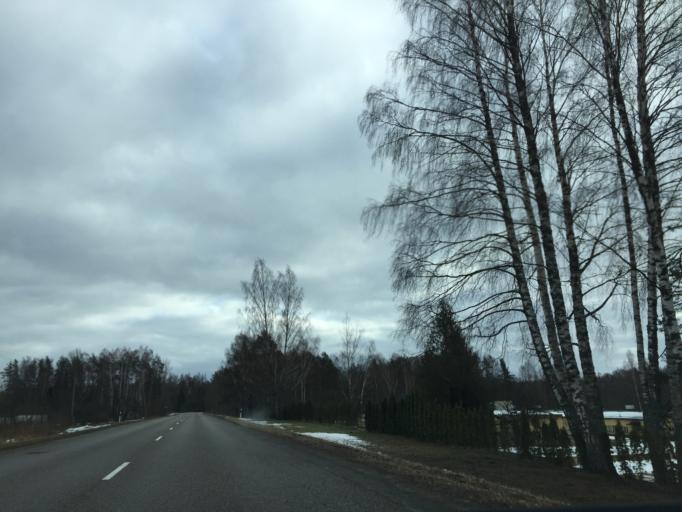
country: LV
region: Salacgrivas
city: Ainazi
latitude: 57.8577
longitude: 24.5116
